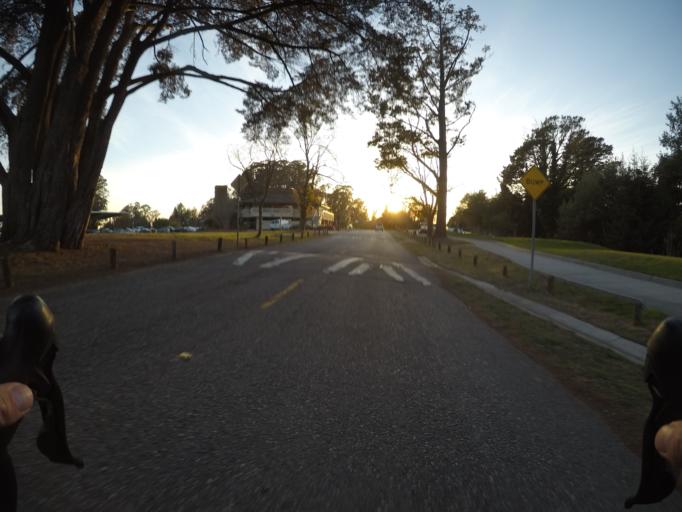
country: US
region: California
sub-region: Santa Cruz County
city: Live Oak
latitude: 36.9979
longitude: -122.0008
